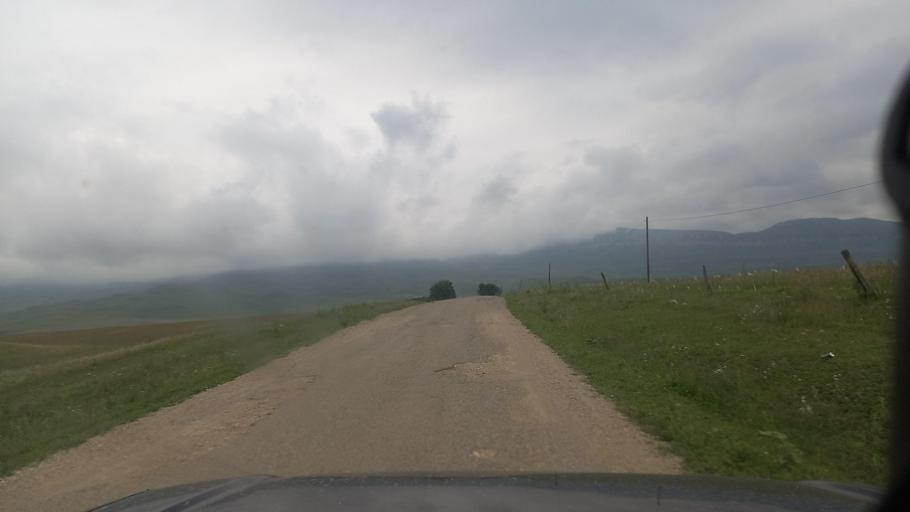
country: RU
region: Karachayevo-Cherkesiya
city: Pregradnaya
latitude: 43.9789
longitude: 41.1988
